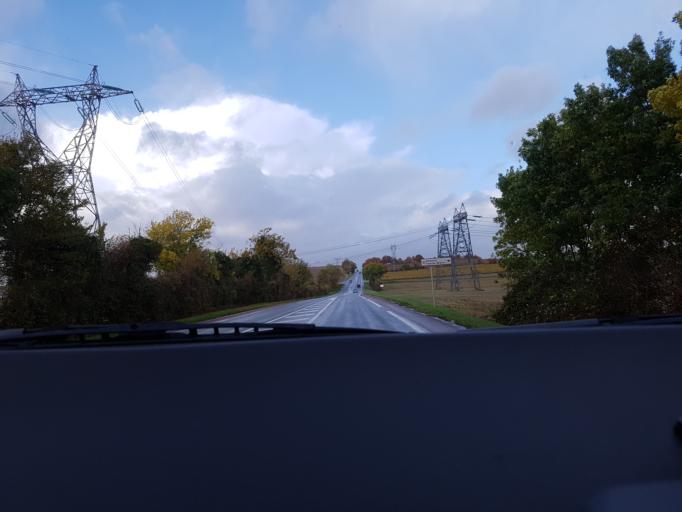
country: FR
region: Poitou-Charentes
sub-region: Departement de la Charente-Maritime
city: Les Gonds
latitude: 45.6728
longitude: -0.6020
